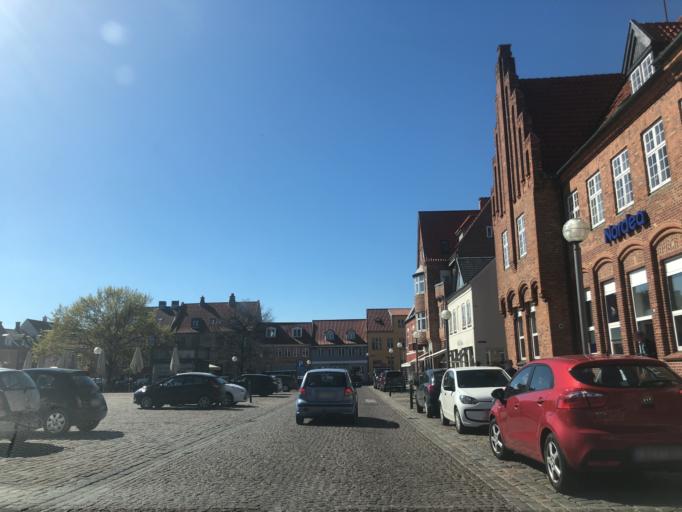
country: DK
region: Zealand
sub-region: Koge Kommune
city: Koge
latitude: 55.4566
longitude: 12.1819
